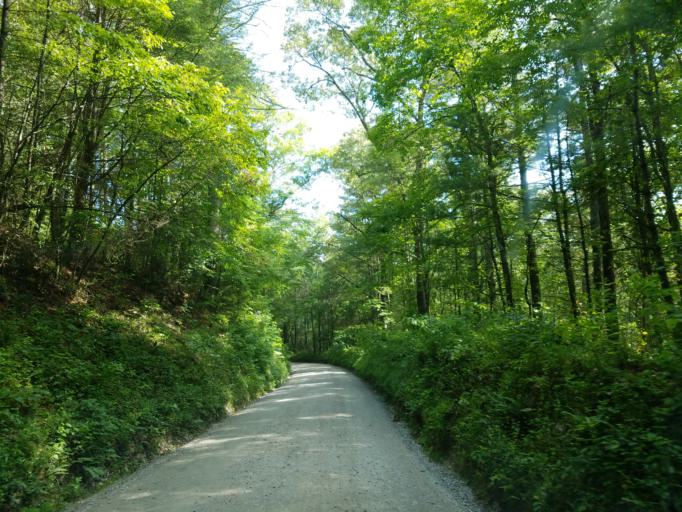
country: US
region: Georgia
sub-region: Fannin County
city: Blue Ridge
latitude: 34.7929
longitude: -84.2431
